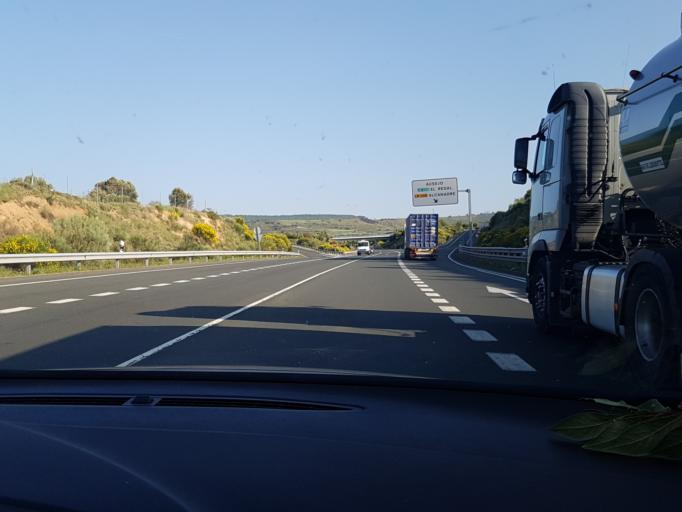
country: ES
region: La Rioja
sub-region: Provincia de La Rioja
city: Ausejo
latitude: 42.3493
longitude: -2.1803
